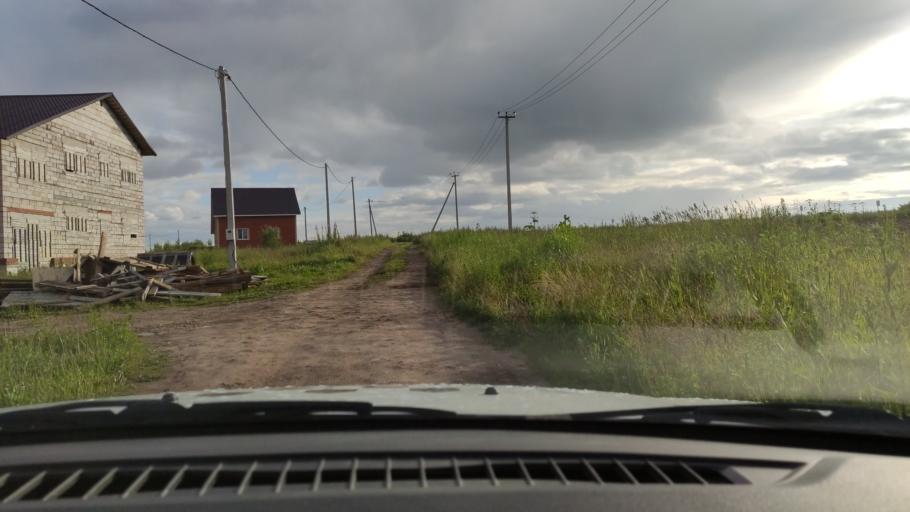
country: RU
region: Perm
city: Perm
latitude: 58.0346
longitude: 56.3784
